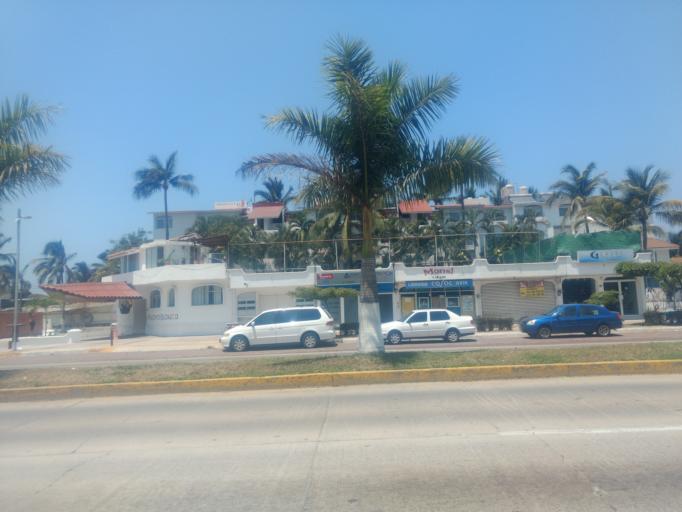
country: MX
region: Colima
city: Tapeixtles
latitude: 19.0870
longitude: -104.3105
